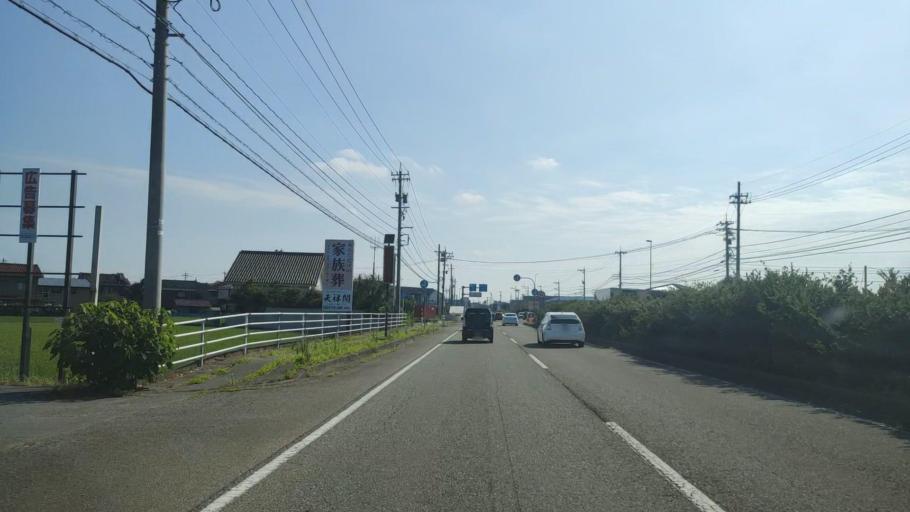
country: JP
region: Ishikawa
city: Matsuto
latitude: 36.5047
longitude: 136.5506
